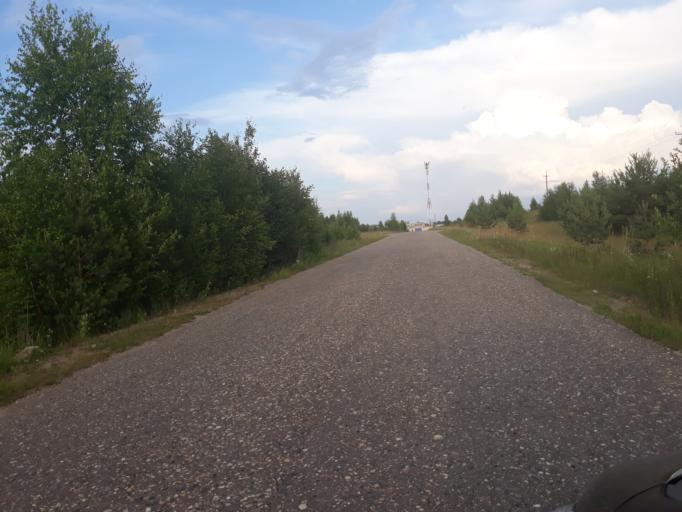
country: RU
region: Jaroslavl
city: Petrovsk
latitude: 56.8740
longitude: 39.0861
